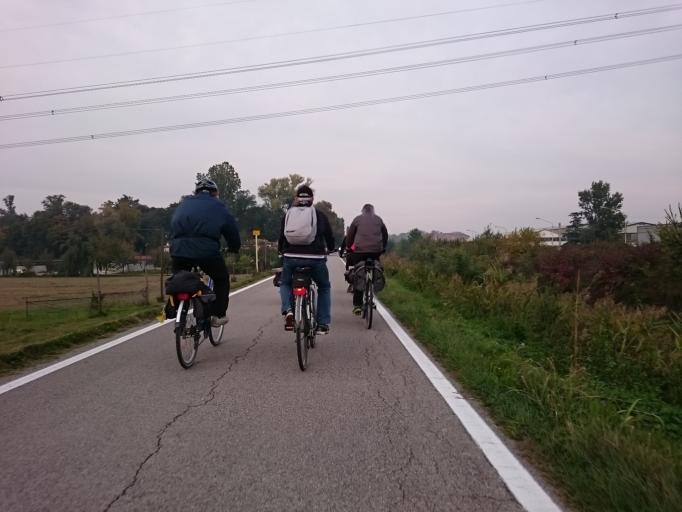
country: IT
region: Veneto
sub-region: Provincia di Padova
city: Mandriola-Sant'Agostino
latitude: 45.3600
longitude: 11.8386
